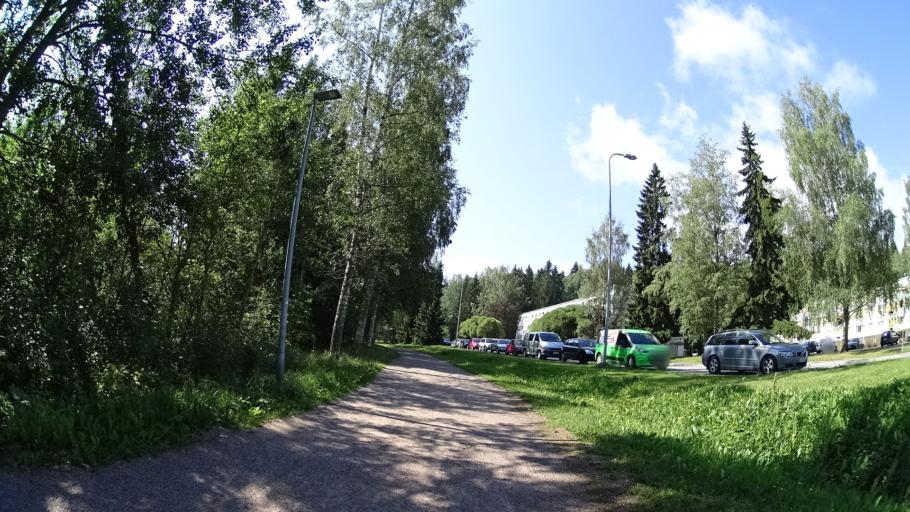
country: FI
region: Uusimaa
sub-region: Helsinki
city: Teekkarikylae
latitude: 60.2717
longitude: 24.8608
